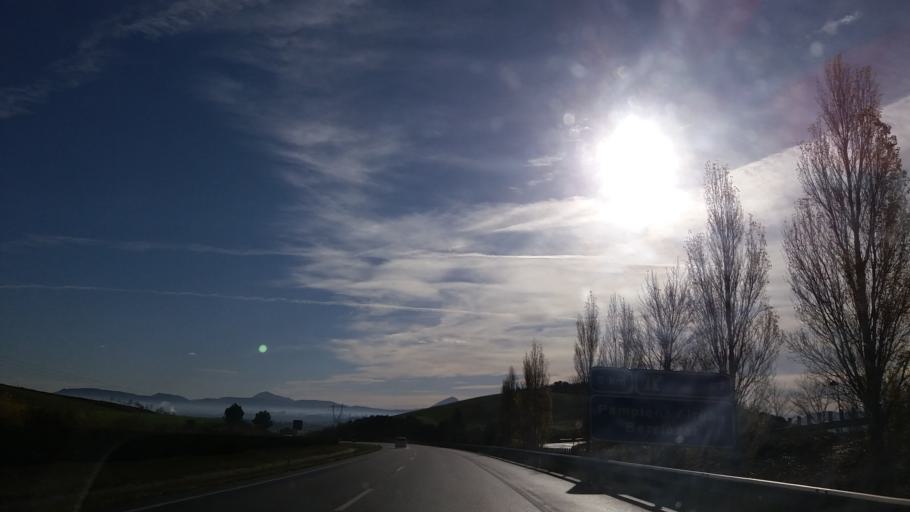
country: ES
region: Navarre
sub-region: Provincia de Navarra
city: Oltza
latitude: 42.8595
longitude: -1.7431
